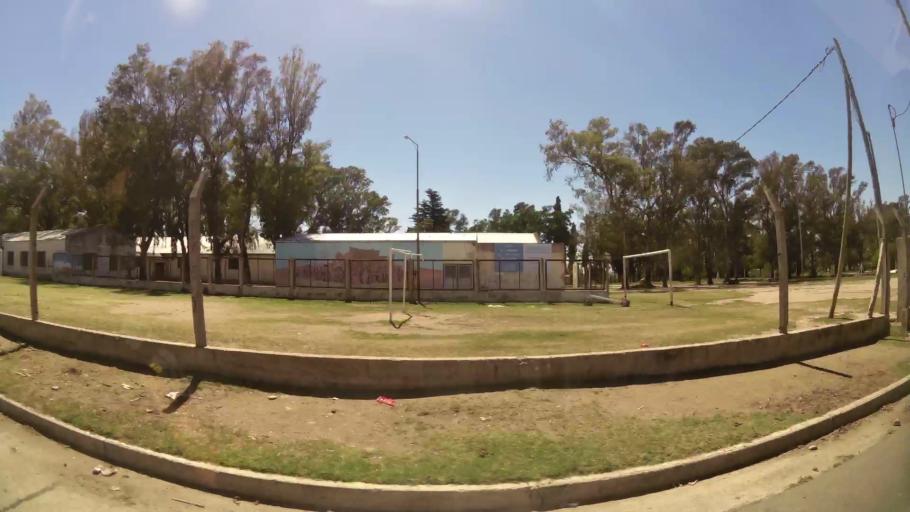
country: AR
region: Cordoba
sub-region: Departamento de Capital
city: Cordoba
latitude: -31.4078
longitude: -64.1345
